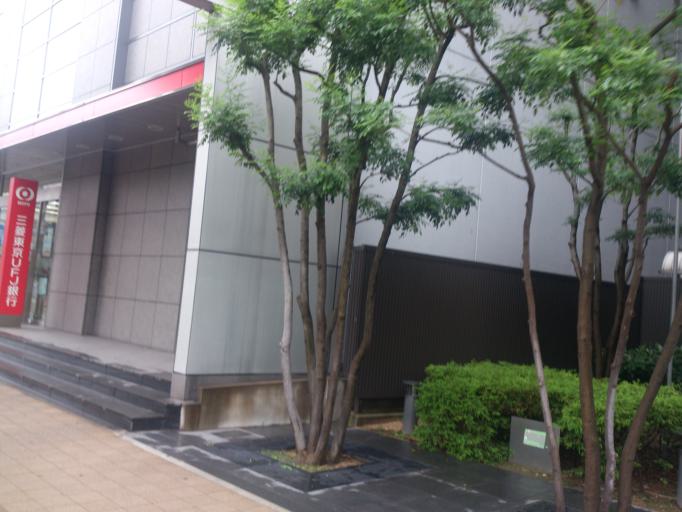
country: JP
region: Hyogo
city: Kobe
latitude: 34.6911
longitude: 135.1959
